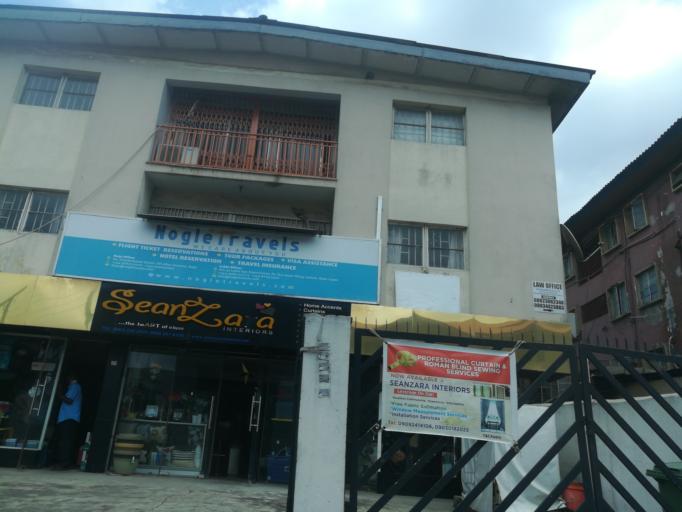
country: NG
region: Lagos
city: Ikeja
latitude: 6.5978
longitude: 3.3517
